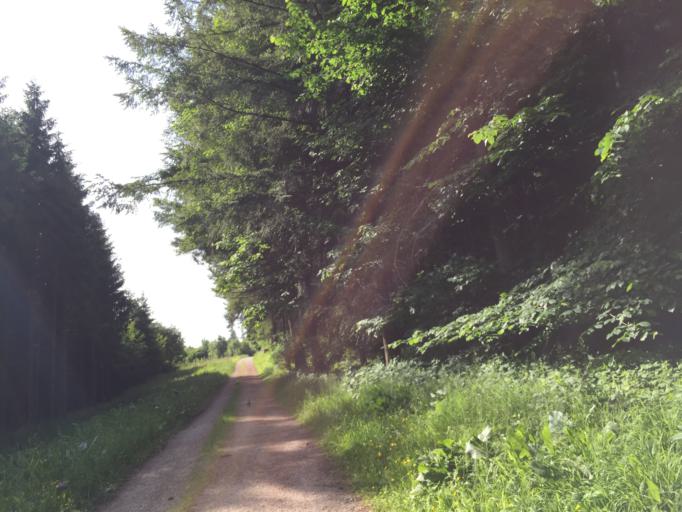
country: CH
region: Bern
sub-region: Bern-Mittelland District
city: Koniz
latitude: 46.9341
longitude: 7.4077
